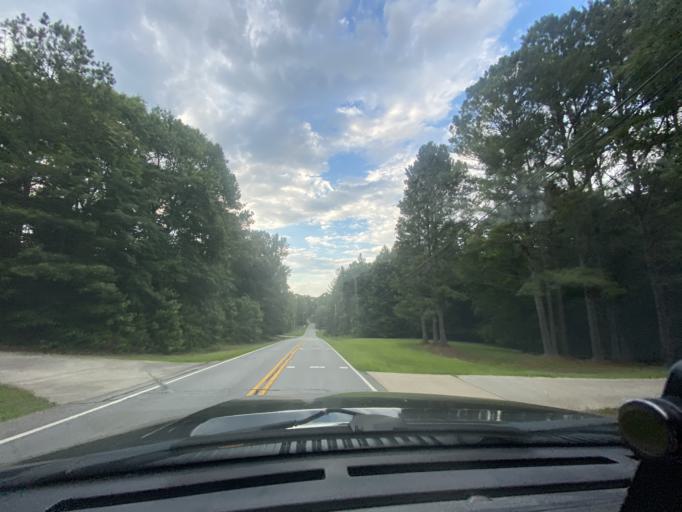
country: US
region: Georgia
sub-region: Fayette County
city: Peachtree City
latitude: 33.4166
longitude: -84.6650
